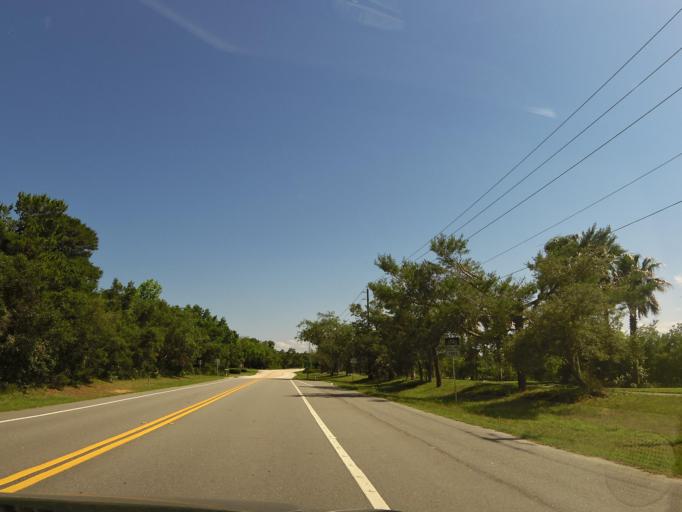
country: US
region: Florida
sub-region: Flagler County
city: Flagler Beach
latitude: 29.4173
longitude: -81.1489
